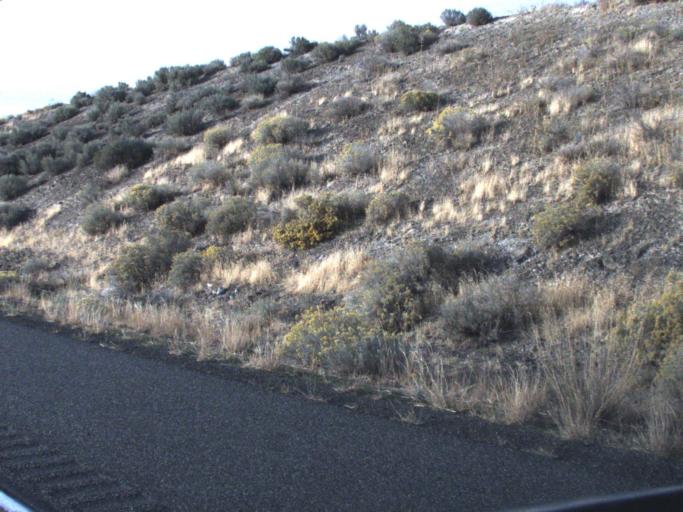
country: US
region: Washington
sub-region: Franklin County
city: West Pasco
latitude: 46.1827
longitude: -119.2444
